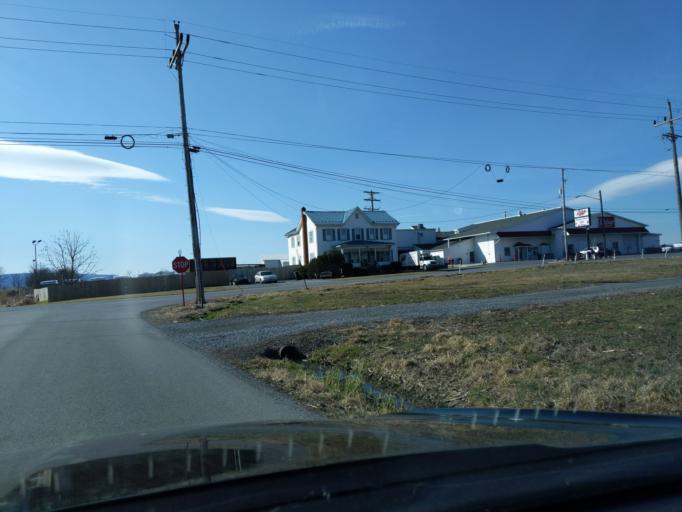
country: US
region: Pennsylvania
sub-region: Blair County
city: Martinsburg
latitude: 40.3030
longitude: -78.3389
